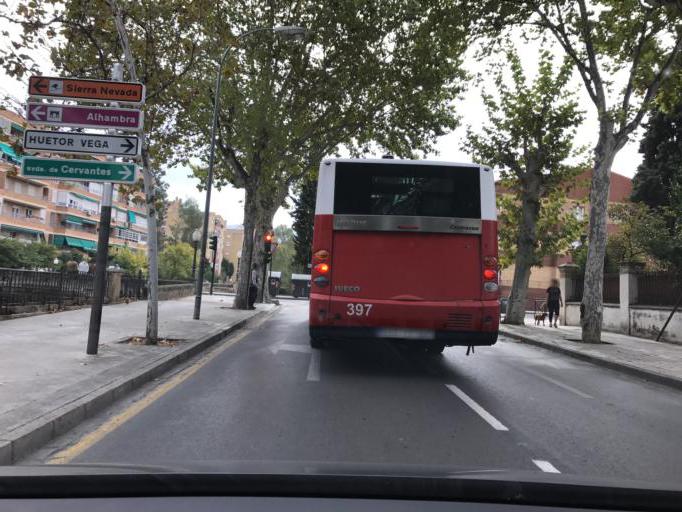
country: ES
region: Andalusia
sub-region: Provincia de Granada
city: Granada
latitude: 37.1673
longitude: -3.5899
